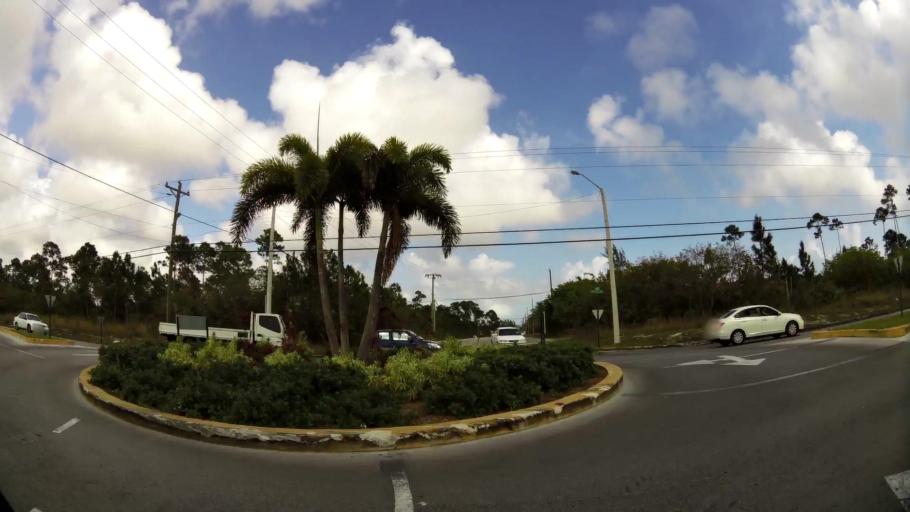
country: BS
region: Freeport
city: Freeport
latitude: 26.5265
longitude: -78.6986
